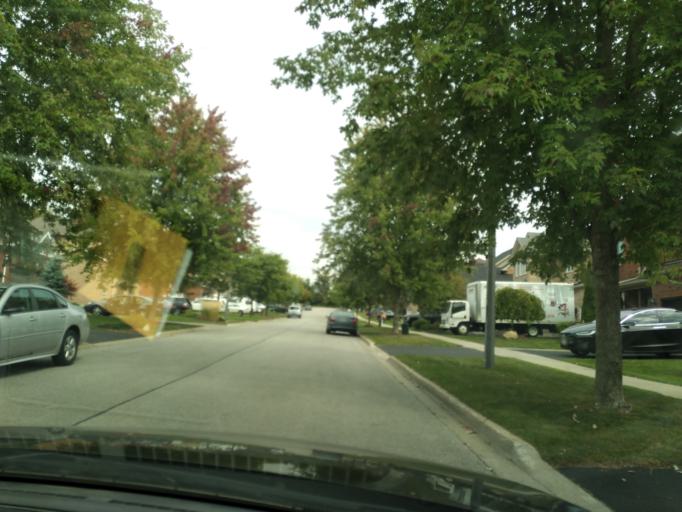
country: CA
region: Ontario
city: Keswick
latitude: 44.2550
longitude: -79.4787
